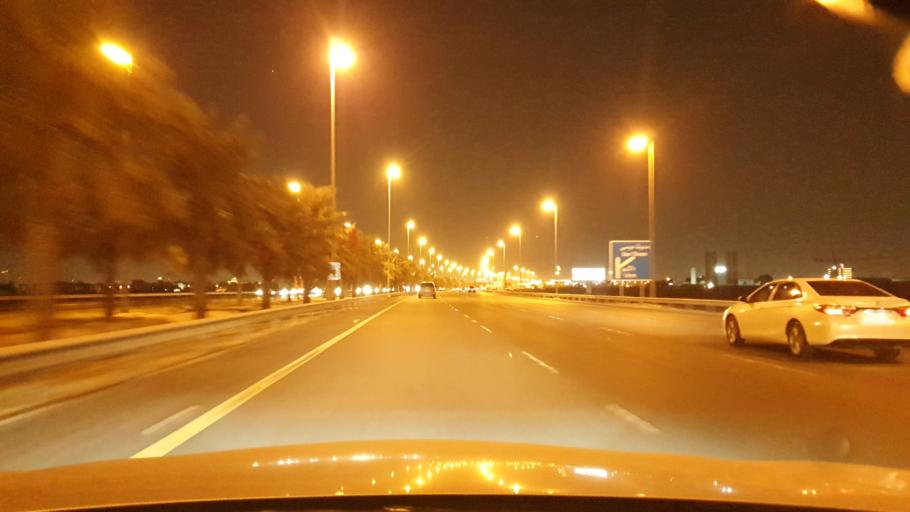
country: BH
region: Northern
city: Madinat `Isa
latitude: 26.1933
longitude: 50.5202
